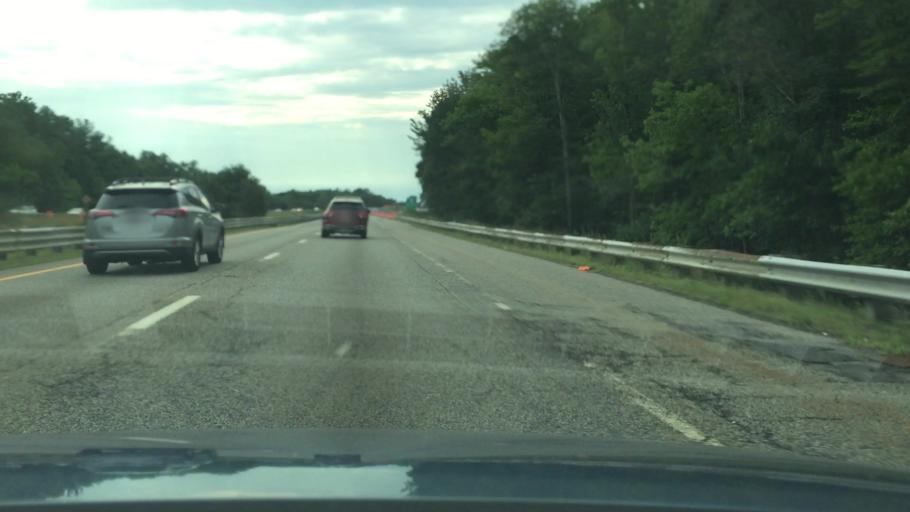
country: US
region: Massachusetts
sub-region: Plymouth County
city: Rockland
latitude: 42.1578
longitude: -70.8669
